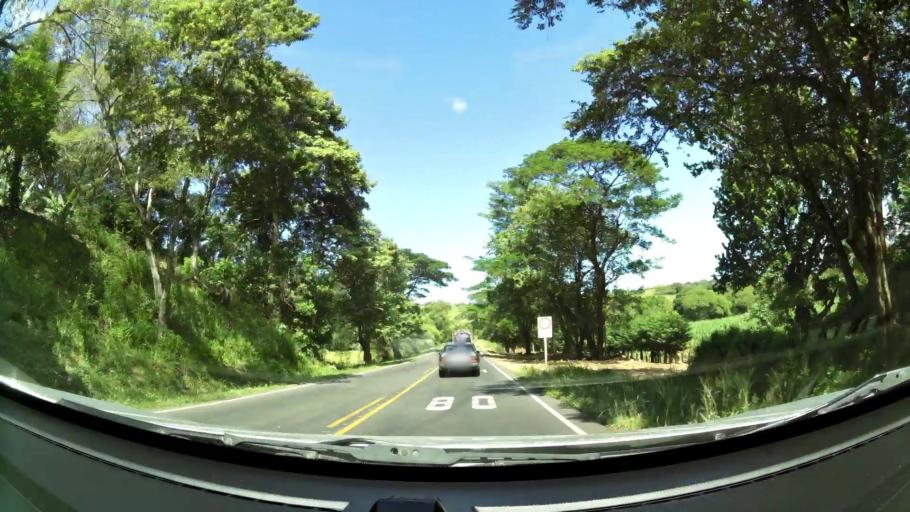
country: CR
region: Guanacaste
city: Juntas
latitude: 10.3193
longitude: -85.0461
